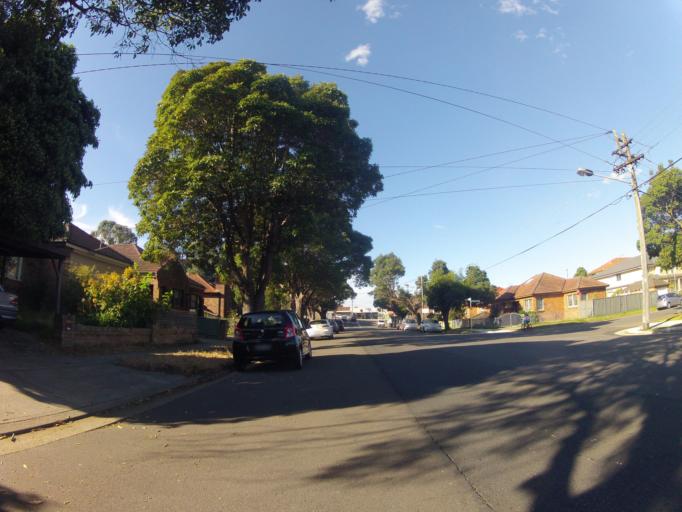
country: AU
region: New South Wales
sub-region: Hurstville
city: Penshurst
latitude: -33.9506
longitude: 151.0799
